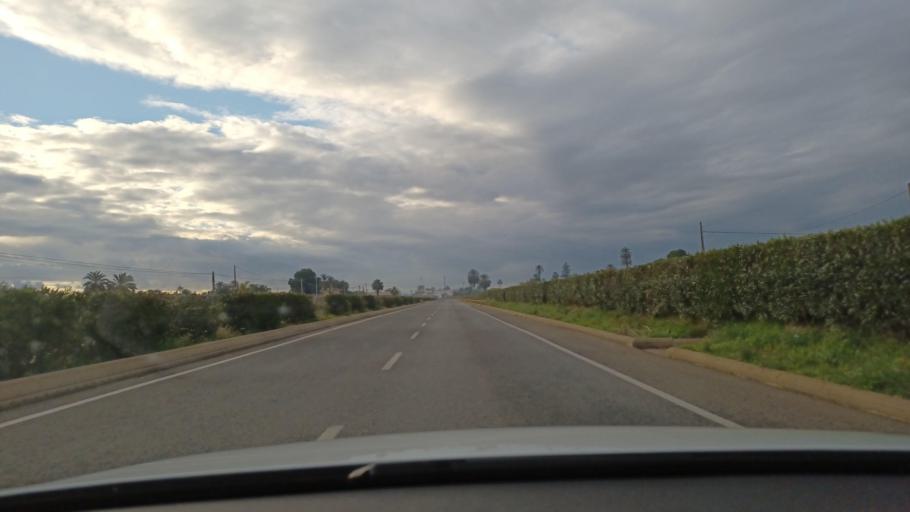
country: ES
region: Valencia
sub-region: Provincia de Alicante
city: Elche
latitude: 38.2290
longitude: -0.6996
